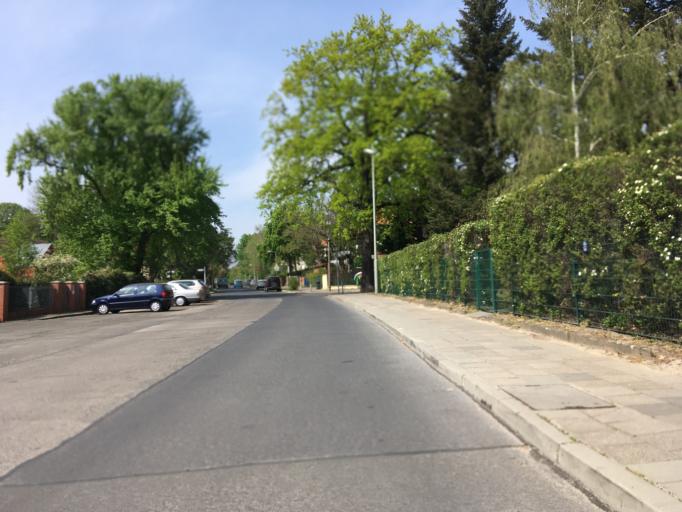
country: DE
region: Berlin
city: Karlshorst
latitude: 52.4853
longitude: 13.5378
